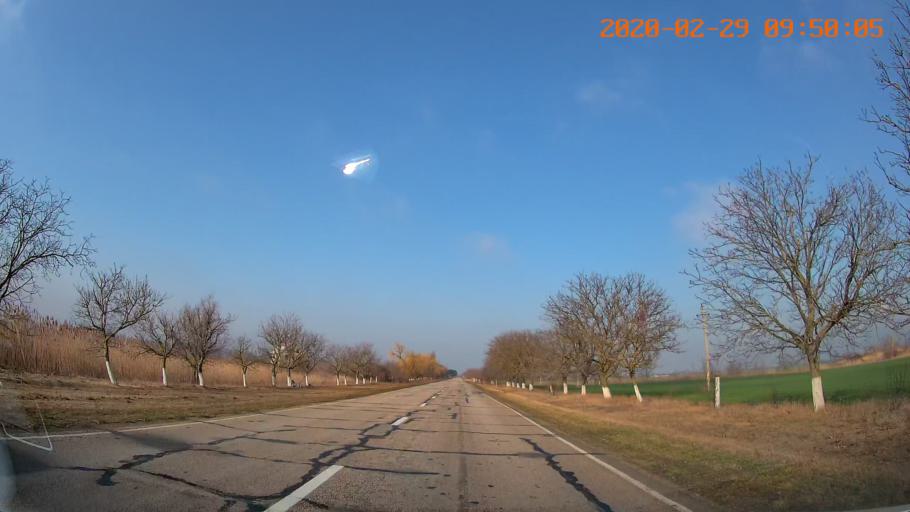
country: MD
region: Telenesti
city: Slobozia
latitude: 46.7010
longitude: 29.7621
